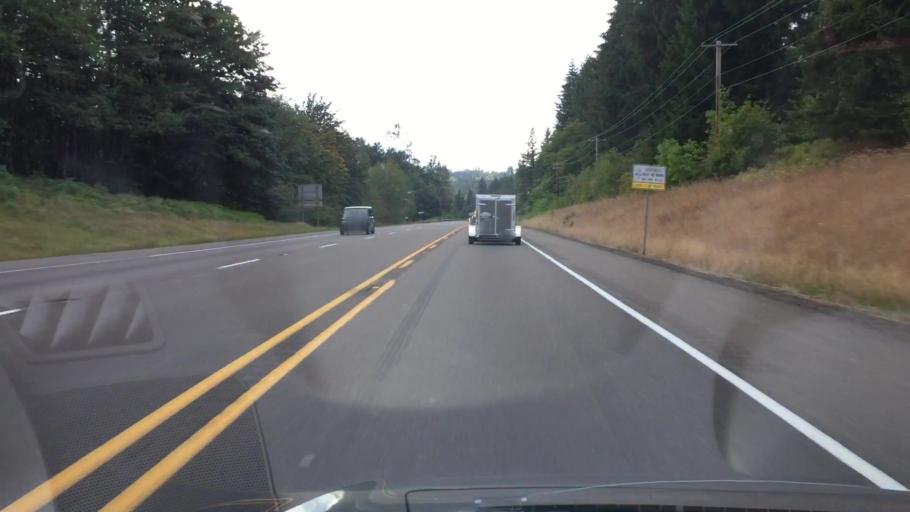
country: US
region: Washington
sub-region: Lewis County
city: Napavine
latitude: 46.5287
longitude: -122.6039
